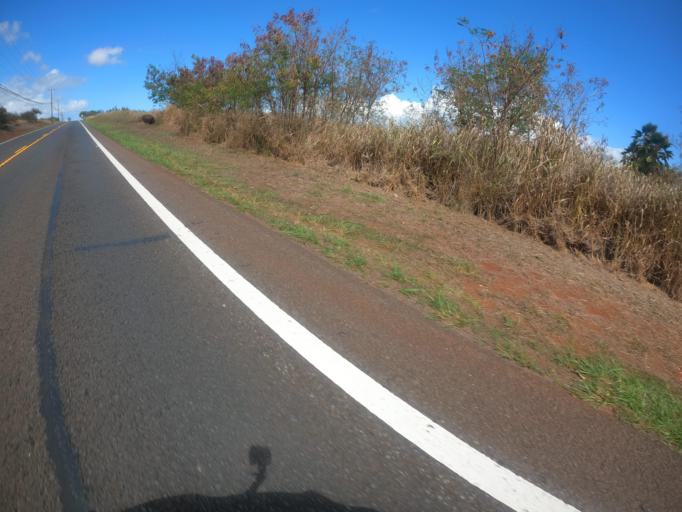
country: US
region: Hawaii
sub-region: Honolulu County
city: Village Park
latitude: 21.4013
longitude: -158.0401
